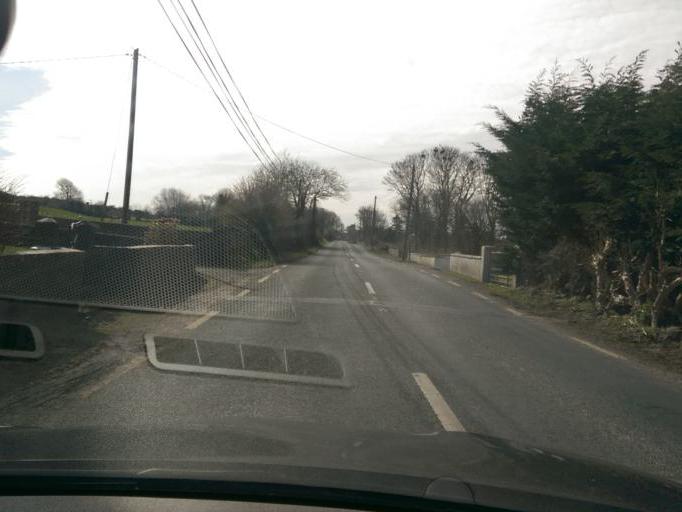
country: IE
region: Connaught
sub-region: County Galway
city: Tuam
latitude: 53.4324
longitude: -8.7561
